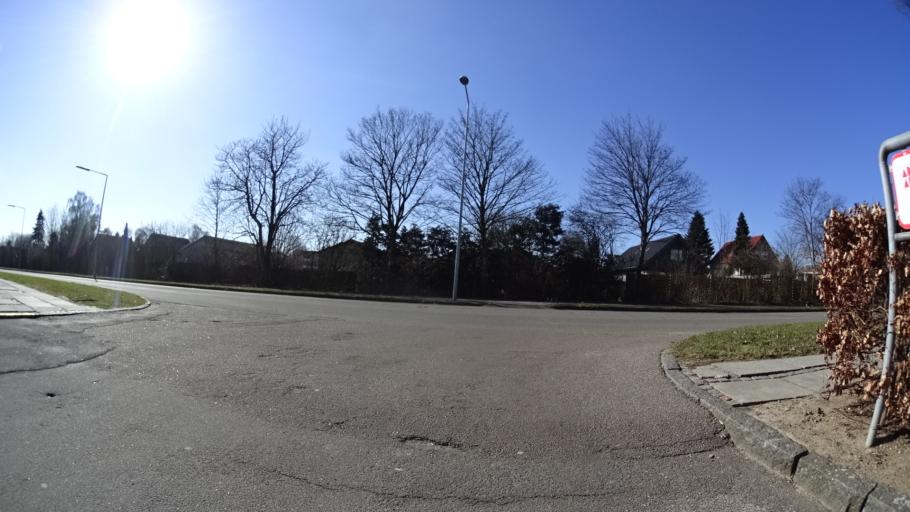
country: DK
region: Central Jutland
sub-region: Arhus Kommune
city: Arhus
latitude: 56.1705
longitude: 10.1726
